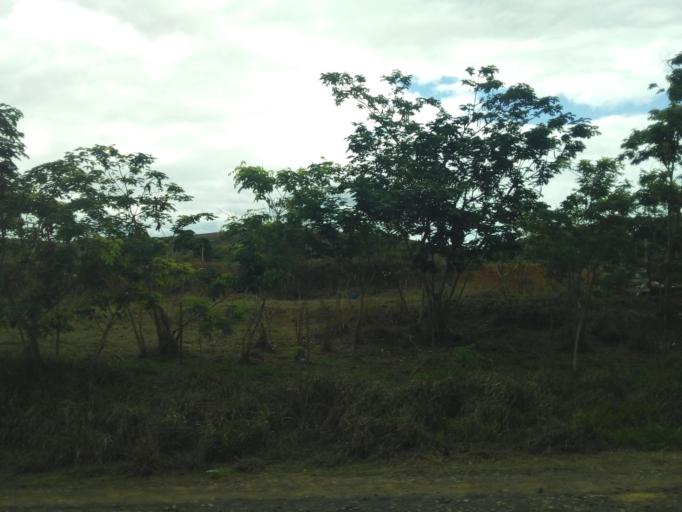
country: BR
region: Minas Gerais
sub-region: Governador Valadares
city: Governador Valadares
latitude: -19.0796
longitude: -42.1597
